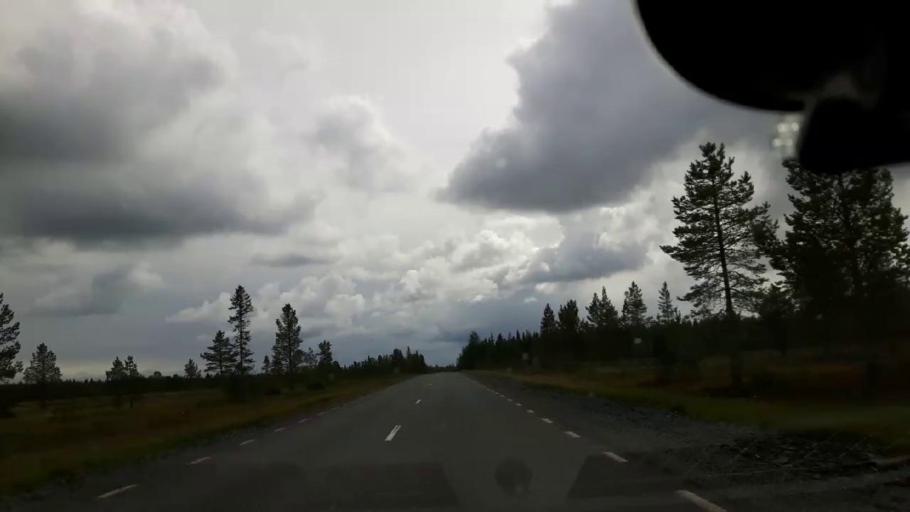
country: SE
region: Jaemtland
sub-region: Krokoms Kommun
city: Valla
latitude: 63.4608
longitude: 13.8270
